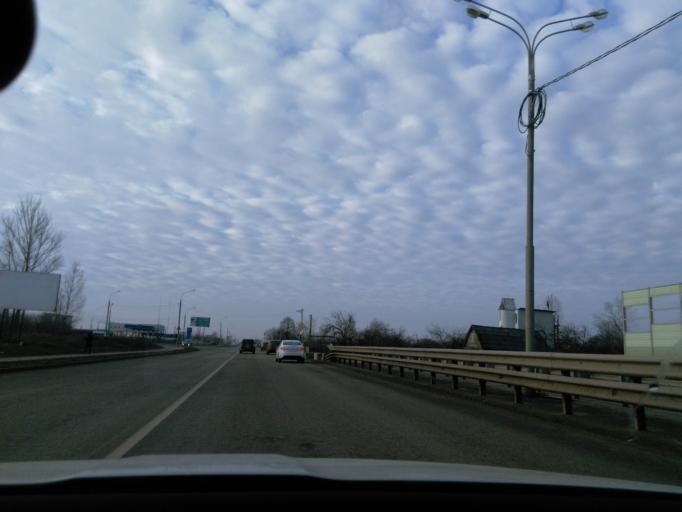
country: RU
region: Moskovskaya
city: Dolgoprudnyy
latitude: 55.9296
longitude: 37.4931
